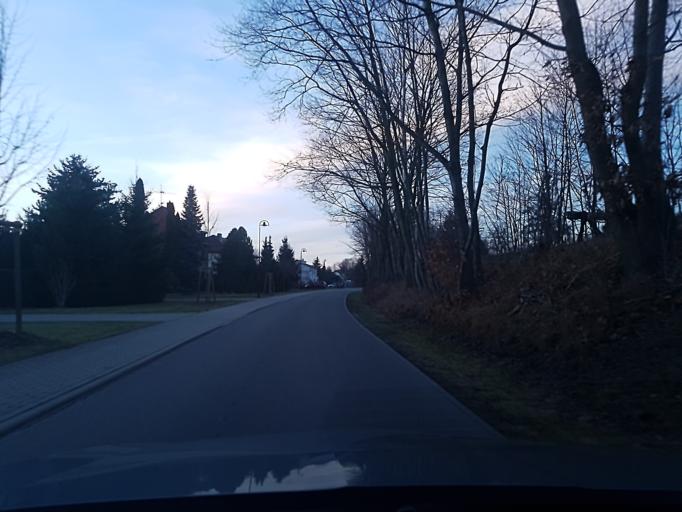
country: DE
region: Brandenburg
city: Finsterwalde
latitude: 51.6350
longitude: 13.6938
